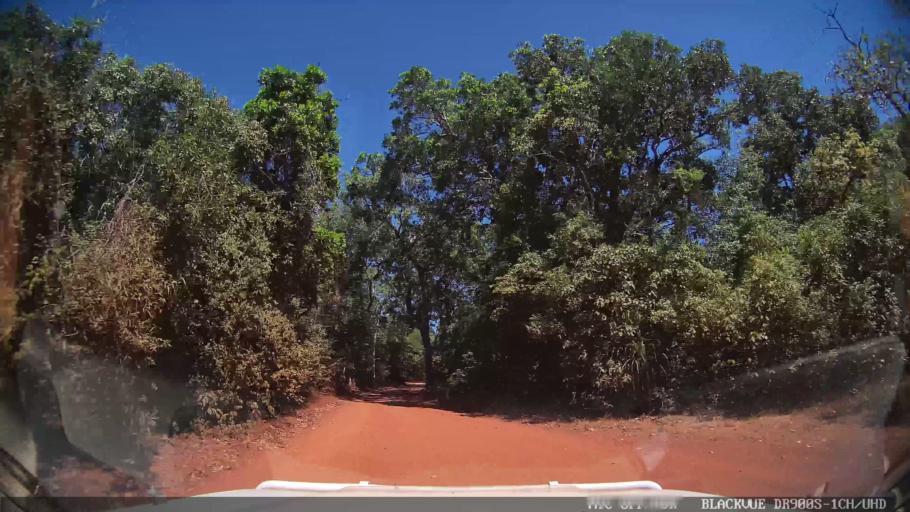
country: AU
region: Queensland
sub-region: Torres
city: Thursday Island
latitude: -10.7084
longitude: 142.5286
